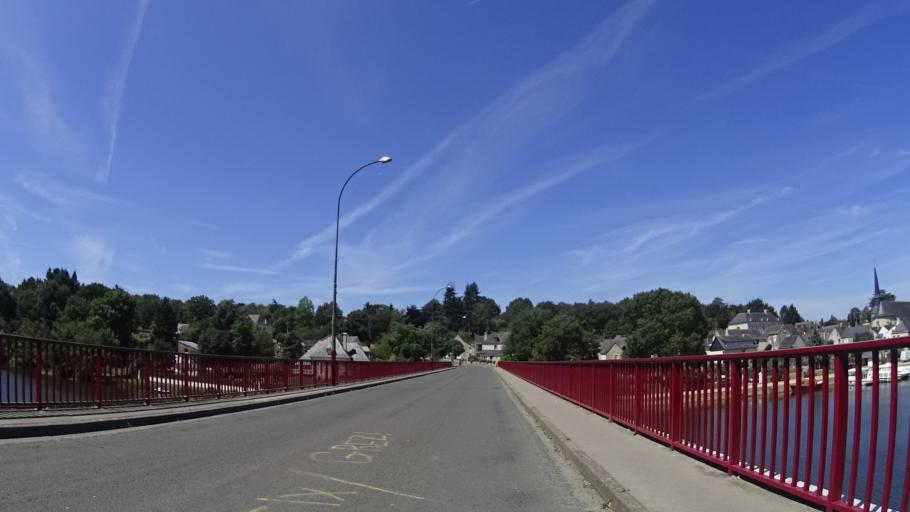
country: FR
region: Pays de la Loire
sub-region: Departement de Maine-et-Loire
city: Grez-Neuville
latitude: 47.6016
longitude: -0.6855
